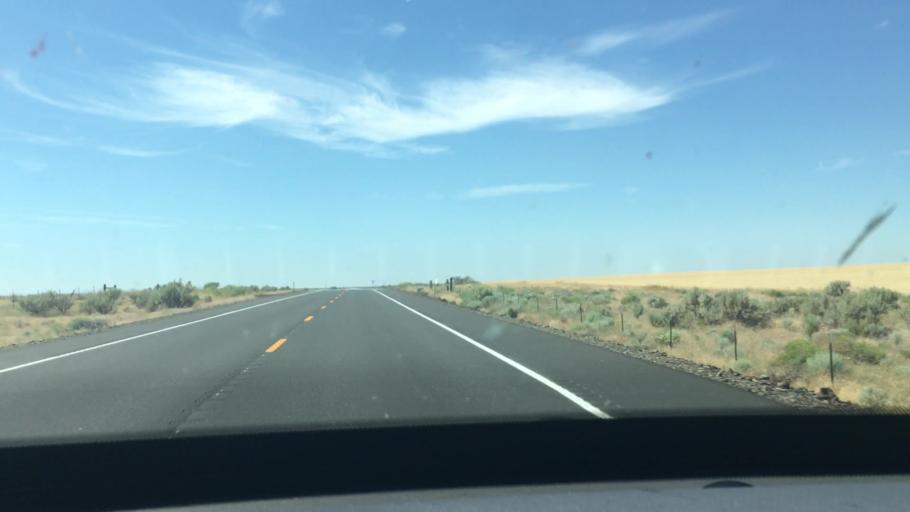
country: US
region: Oregon
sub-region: Sherman County
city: Moro
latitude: 45.1675
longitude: -120.6924
